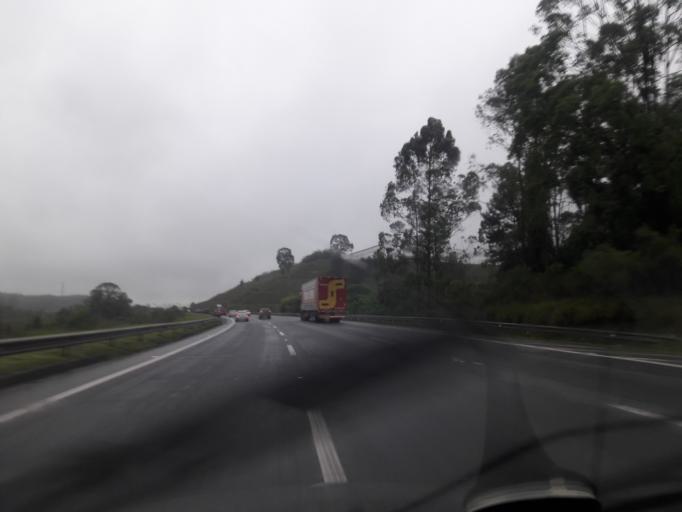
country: BR
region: Sao Paulo
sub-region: Embu
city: Embu
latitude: -23.6547
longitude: -46.8308
